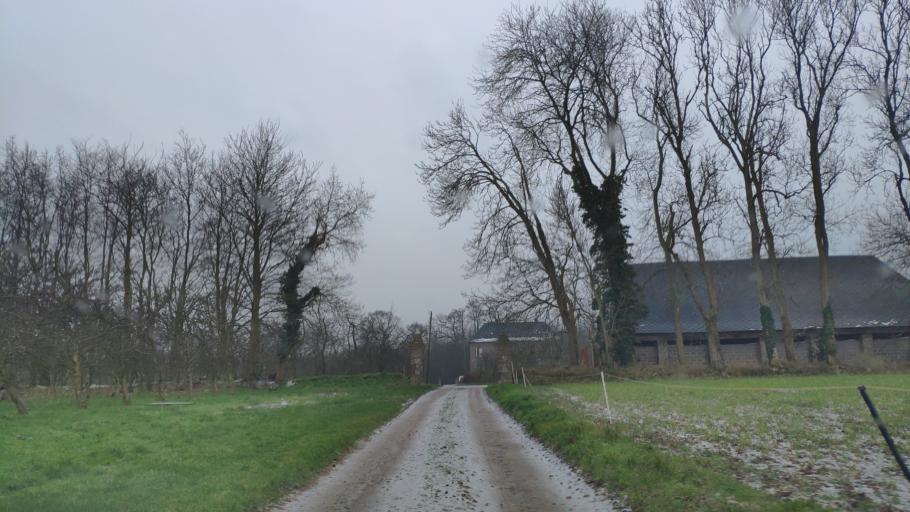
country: FR
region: Haute-Normandie
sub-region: Departement de la Seine-Maritime
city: Neville
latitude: 49.7924
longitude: 0.7000
